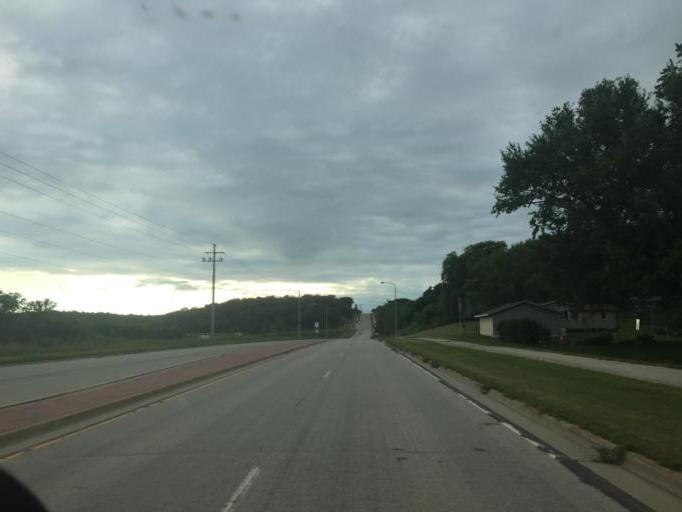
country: US
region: Minnesota
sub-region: Olmsted County
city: Rochester
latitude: 43.9640
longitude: -92.4713
